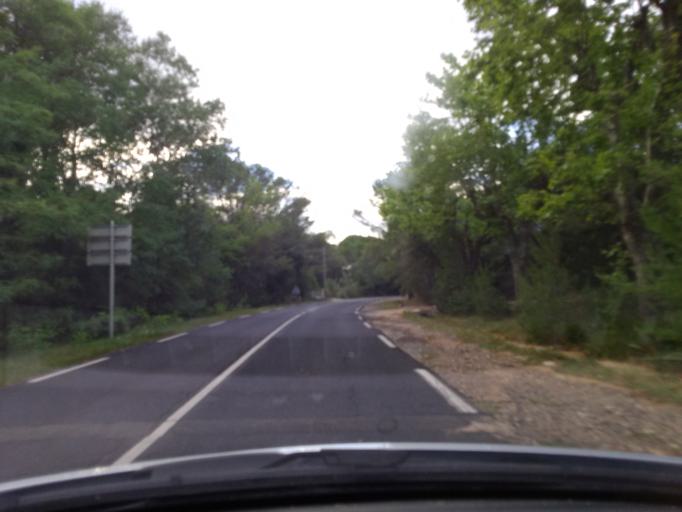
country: FR
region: Languedoc-Roussillon
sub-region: Departement de l'Herault
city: Nebian
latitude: 43.6409
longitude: 3.4112
